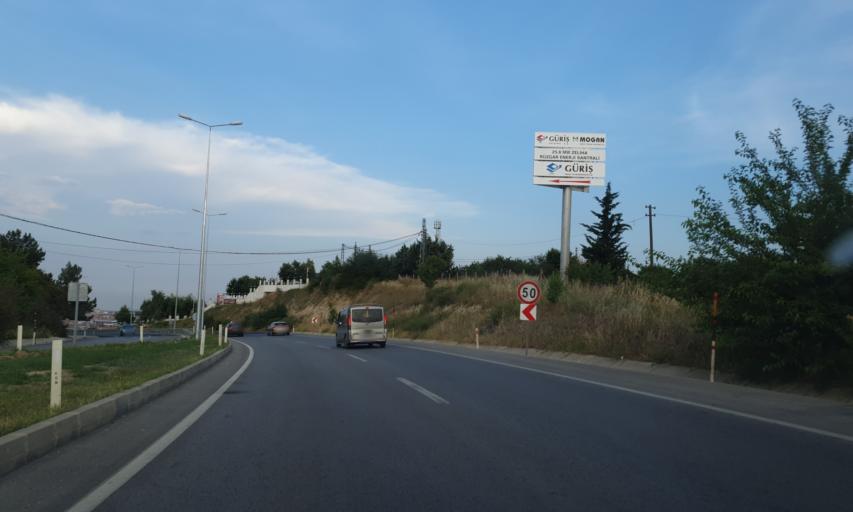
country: TR
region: Kirklareli
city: Luleburgaz
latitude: 41.4040
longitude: 27.3290
